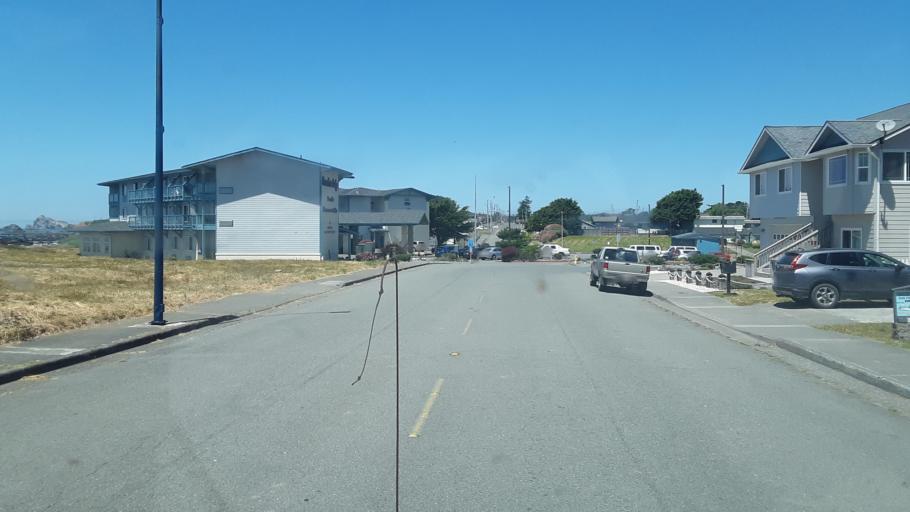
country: US
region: California
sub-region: Del Norte County
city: Crescent City
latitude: 41.7471
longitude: -124.2024
